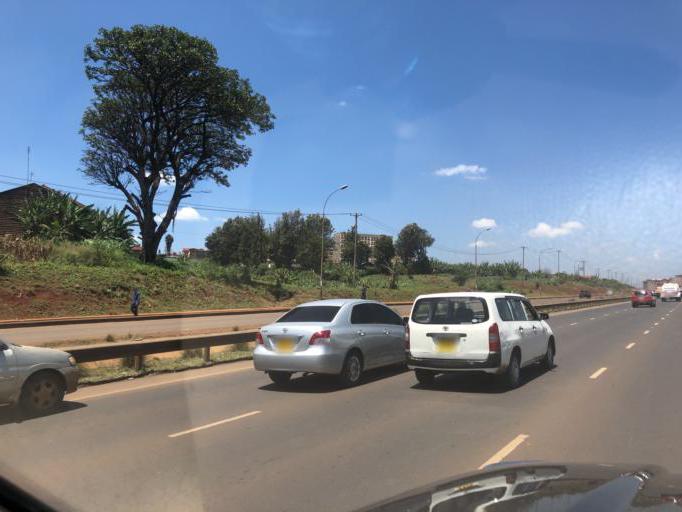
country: KE
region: Kiambu
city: Kiambu
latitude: -1.2126
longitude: 36.9027
